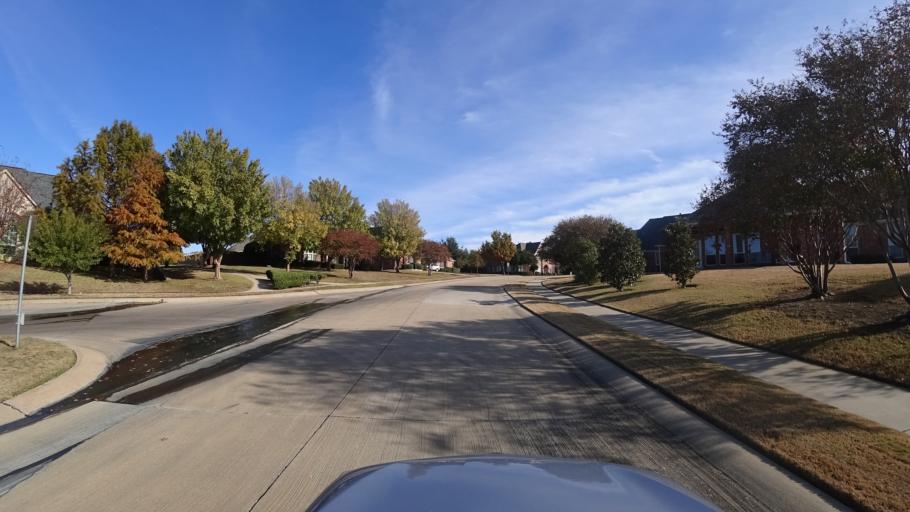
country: US
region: Texas
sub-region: Denton County
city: The Colony
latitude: 33.0385
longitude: -96.8959
